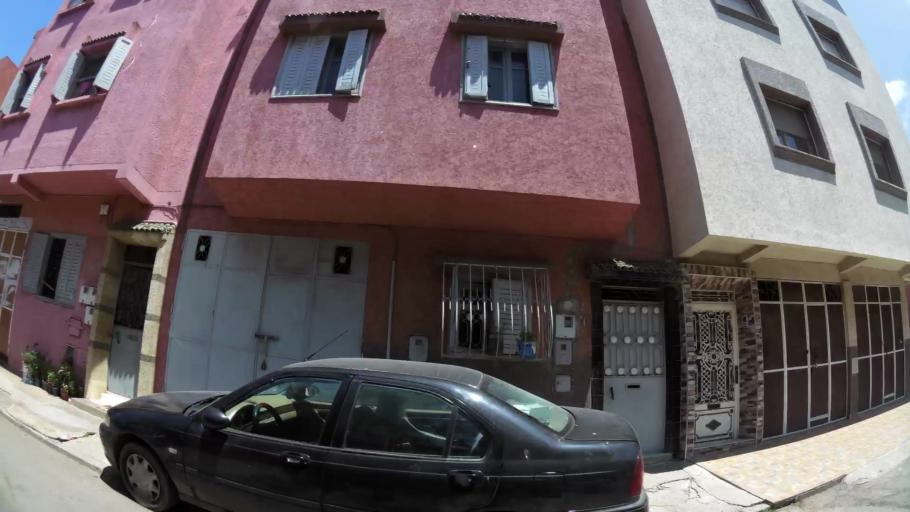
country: MA
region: Gharb-Chrarda-Beni Hssen
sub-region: Kenitra Province
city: Kenitra
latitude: 34.2655
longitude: -6.5563
